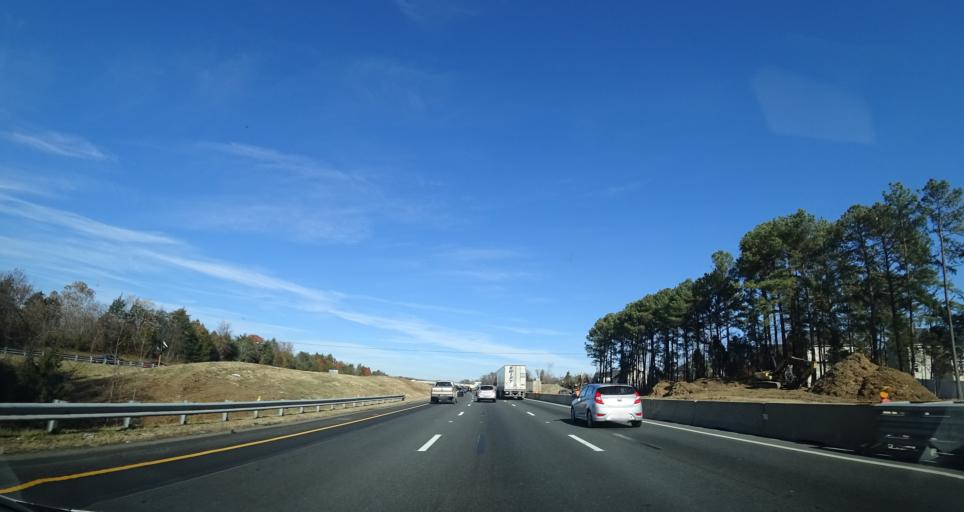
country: US
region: Virginia
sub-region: Stafford County
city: Falmouth
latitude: 38.3079
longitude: -77.5018
